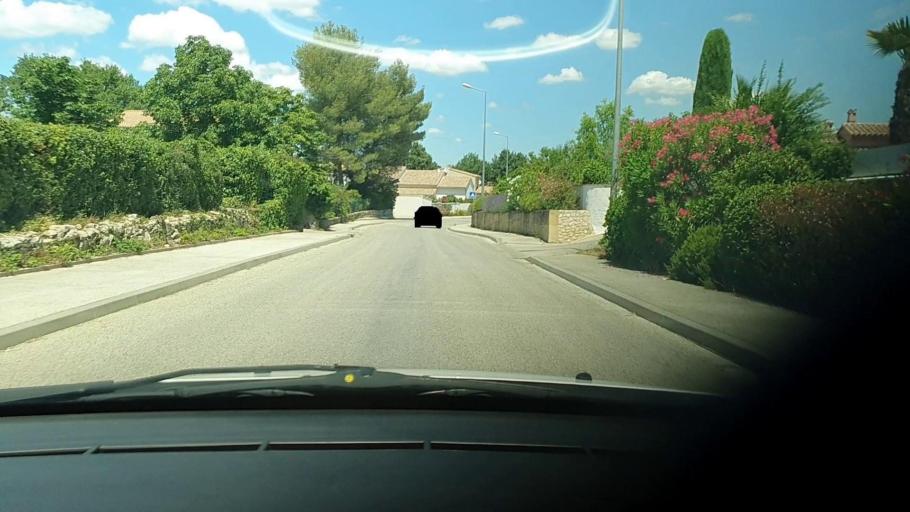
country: FR
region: Languedoc-Roussillon
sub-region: Departement du Gard
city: Blauzac
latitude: 43.9679
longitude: 4.3660
